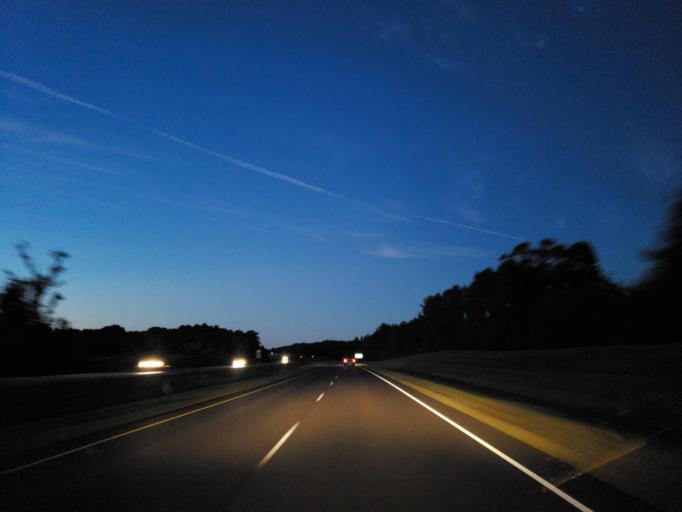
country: US
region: Mississippi
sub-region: Clarke County
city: Quitman
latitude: 32.0436
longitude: -88.6778
